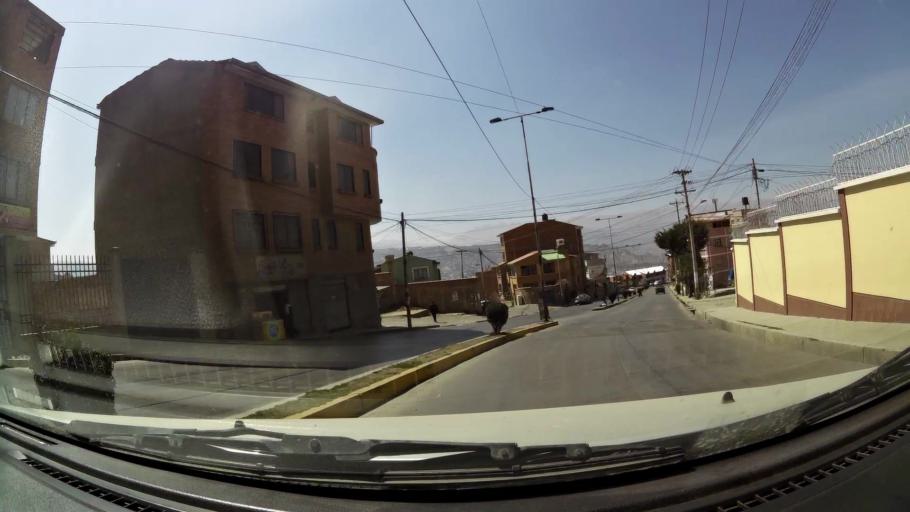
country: BO
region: La Paz
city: La Paz
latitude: -16.5299
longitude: -68.1291
